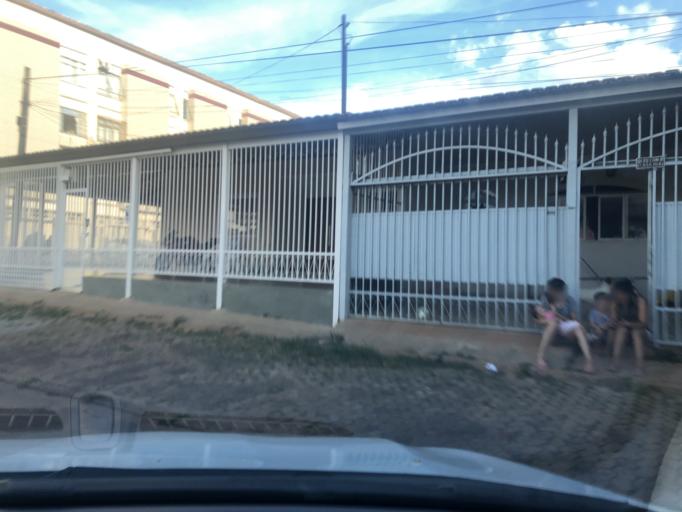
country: BR
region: Federal District
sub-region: Brasilia
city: Brasilia
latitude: -15.8252
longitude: -47.9871
